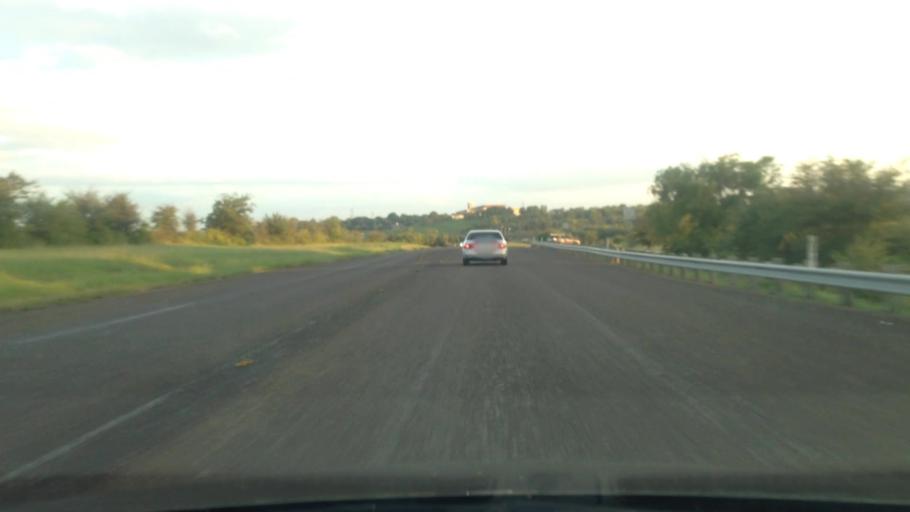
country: US
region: Texas
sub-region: Tarrant County
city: Benbrook
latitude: 32.6835
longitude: -97.4991
